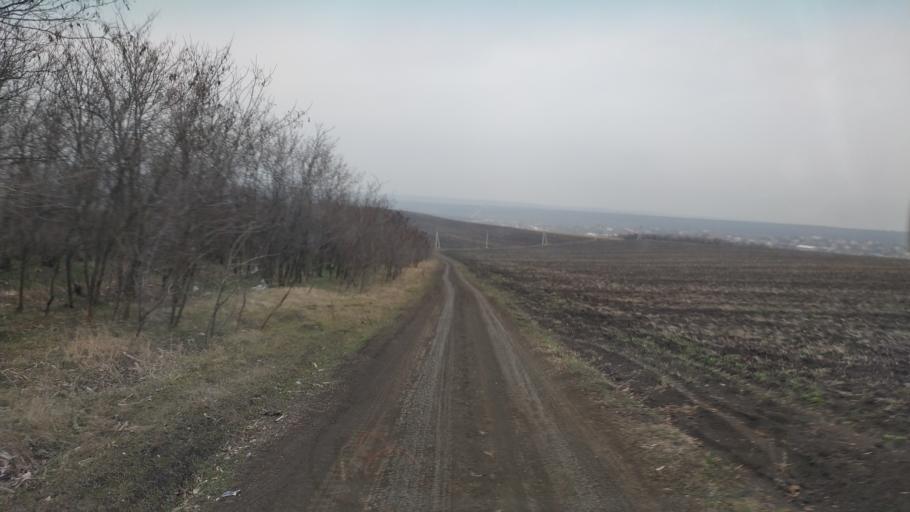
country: MD
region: Chisinau
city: Singera
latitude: 46.8239
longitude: 28.9846
